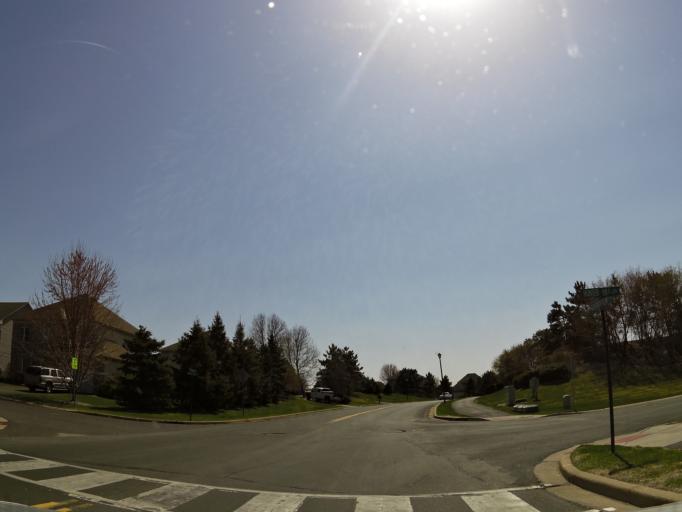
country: US
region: Wisconsin
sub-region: Saint Croix County
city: Hudson
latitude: 44.9745
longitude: -92.7309
